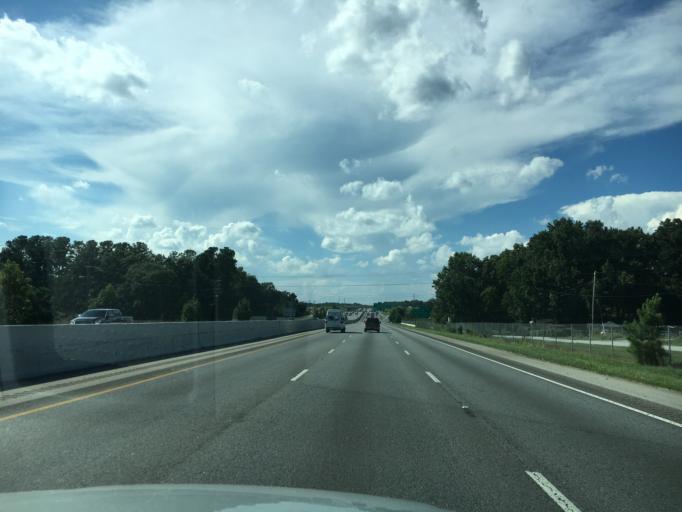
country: US
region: South Carolina
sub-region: Greenville County
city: Simpsonville
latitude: 34.7311
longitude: -82.2659
